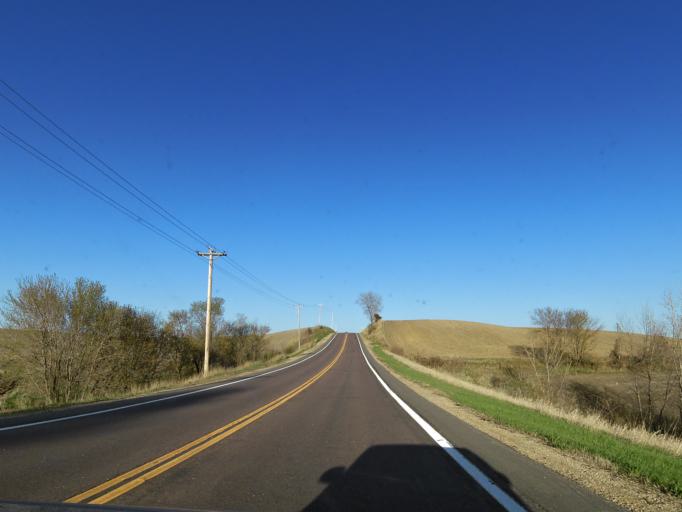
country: US
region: Minnesota
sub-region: Goodhue County
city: Cannon Falls
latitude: 44.6011
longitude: -92.8798
